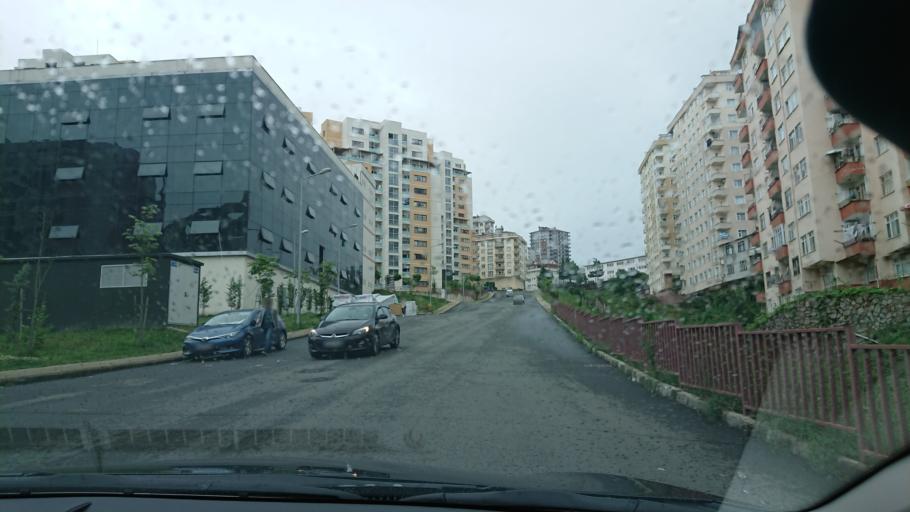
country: TR
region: Rize
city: Rize
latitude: 41.0174
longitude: 40.5157
